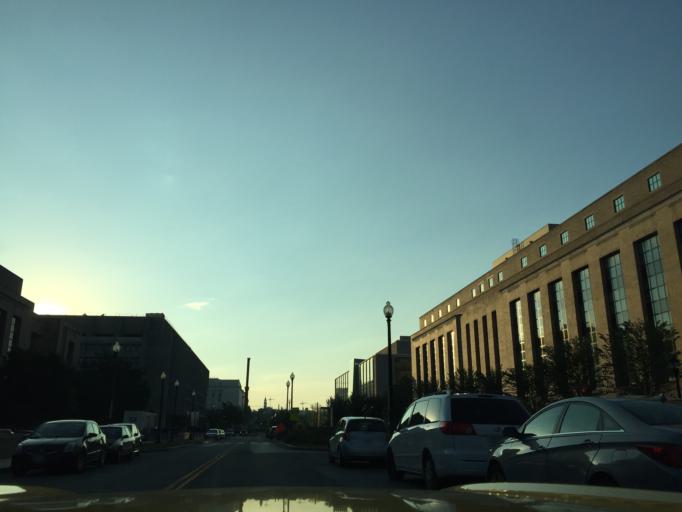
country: US
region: Washington, D.C.
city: Washington, D.C.
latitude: 38.8860
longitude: -77.0171
